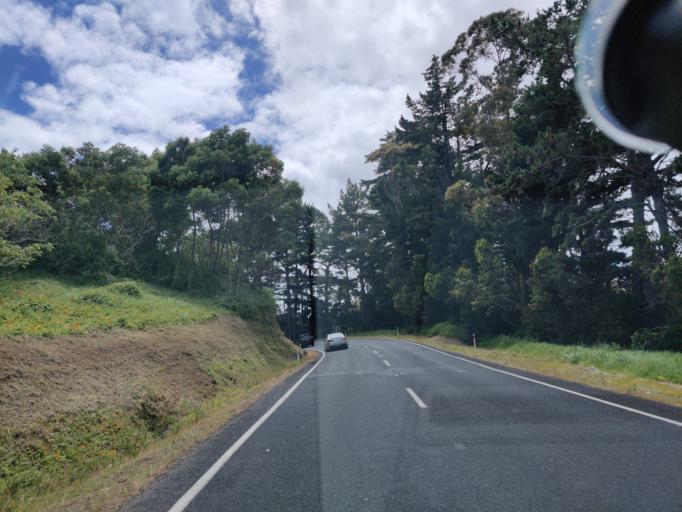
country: NZ
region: Northland
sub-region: Far North District
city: Kaitaia
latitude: -34.9513
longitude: 173.1866
